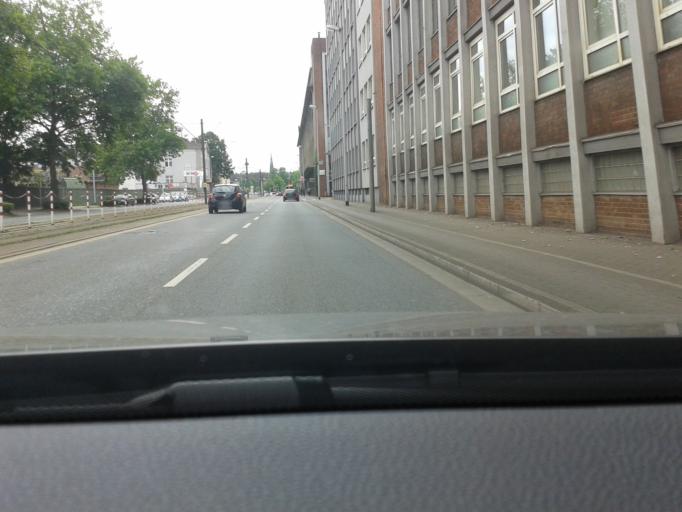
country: DE
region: North Rhine-Westphalia
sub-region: Regierungsbezirk Dusseldorf
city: Muelheim (Ruhr)
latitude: 51.4353
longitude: 6.8748
